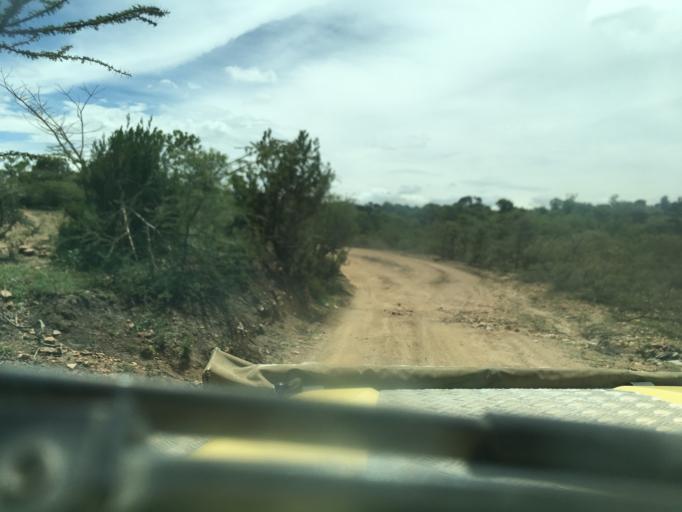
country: TZ
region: Mara
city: Mugumu
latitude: -1.9227
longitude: 35.4306
